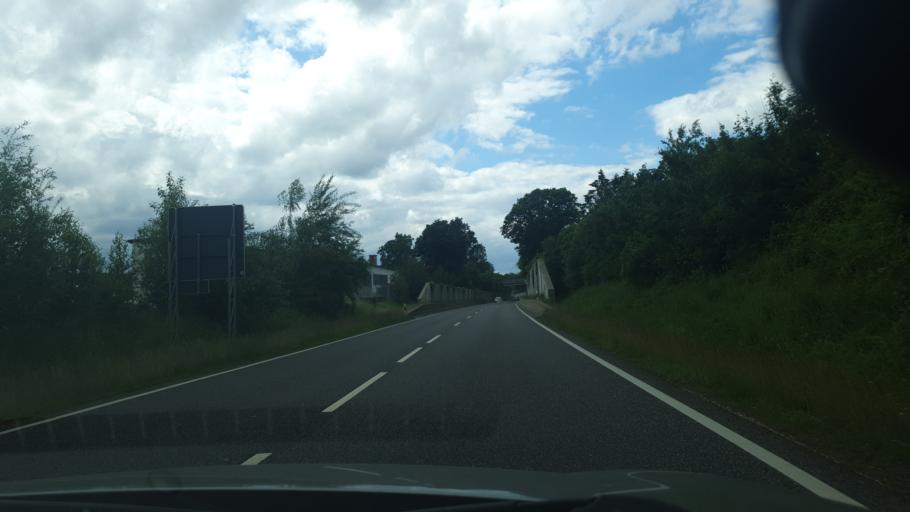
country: DE
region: Rheinland-Pfalz
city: Hohr-Grenzhausen
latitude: 50.4333
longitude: 7.6814
